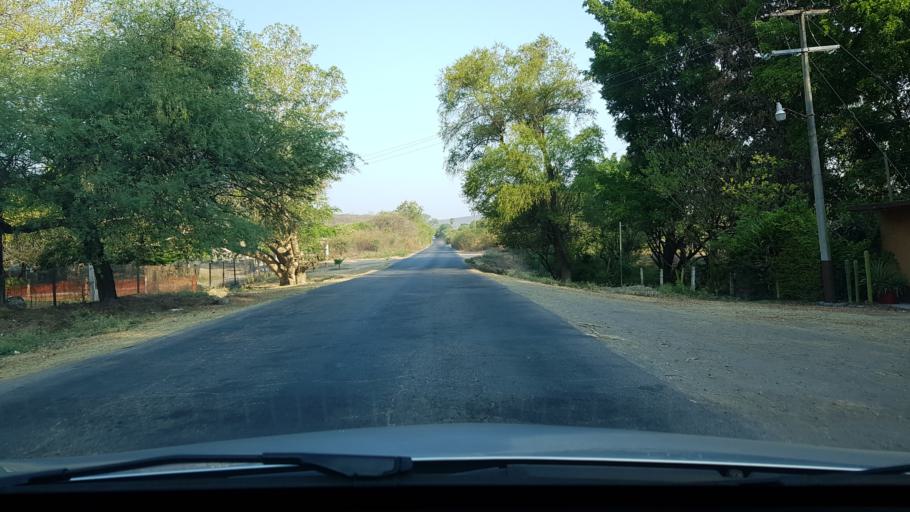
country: MX
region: Morelos
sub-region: Tepalcingo
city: Zacapalco
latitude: 18.6452
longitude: -99.0227
